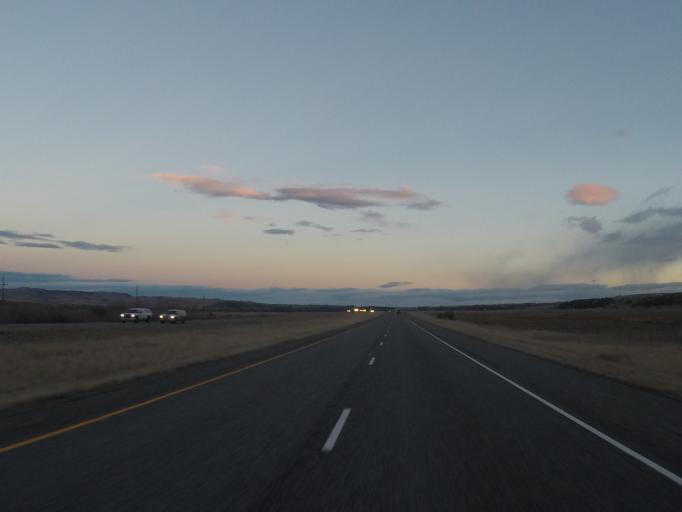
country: US
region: Montana
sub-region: Sweet Grass County
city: Big Timber
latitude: 45.7912
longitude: -109.8292
